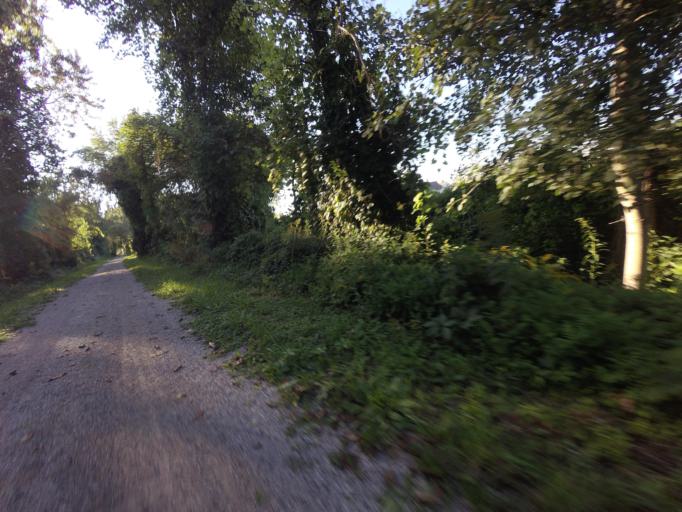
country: CA
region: Ontario
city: Goderich
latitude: 43.7557
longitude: -81.6772
